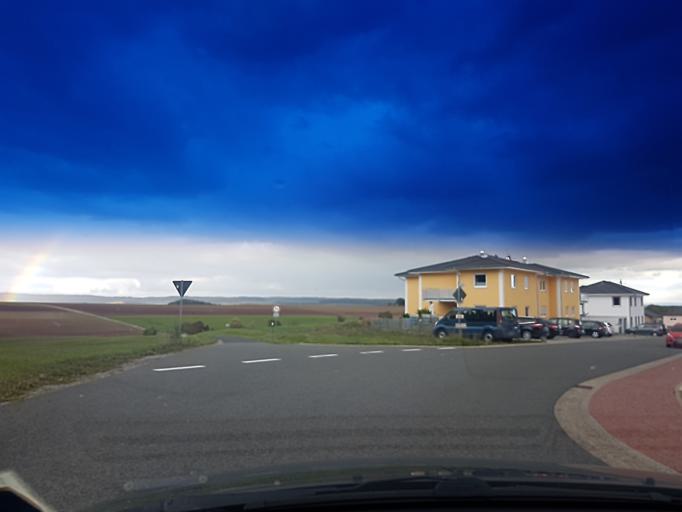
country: DE
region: Bavaria
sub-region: Regierungsbezirk Mittelfranken
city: Burghaslach
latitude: 49.7386
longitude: 10.6057
